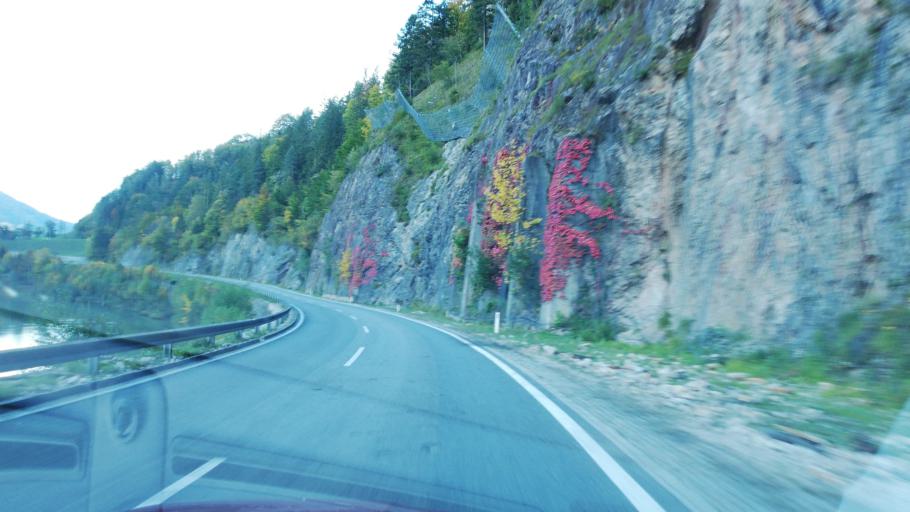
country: AT
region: Styria
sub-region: Politischer Bezirk Liezen
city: Altenmarkt bei Sankt Gallen
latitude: 47.7775
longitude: 14.6539
